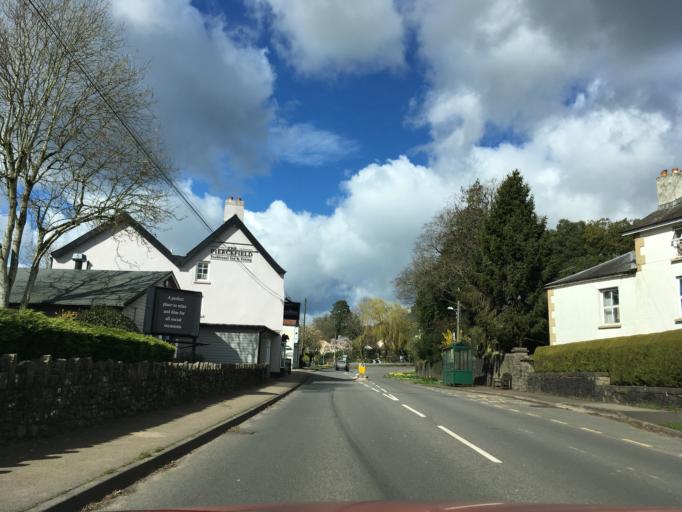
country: GB
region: Wales
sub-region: Monmouthshire
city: Chepstow
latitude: 51.6638
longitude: -2.6968
